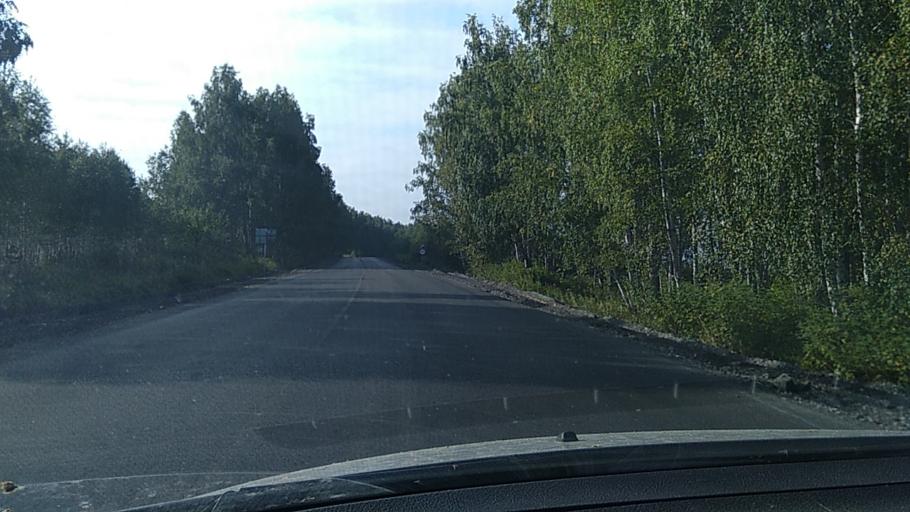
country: RU
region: Chelyabinsk
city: Karabash
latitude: 55.3754
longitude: 60.2507
